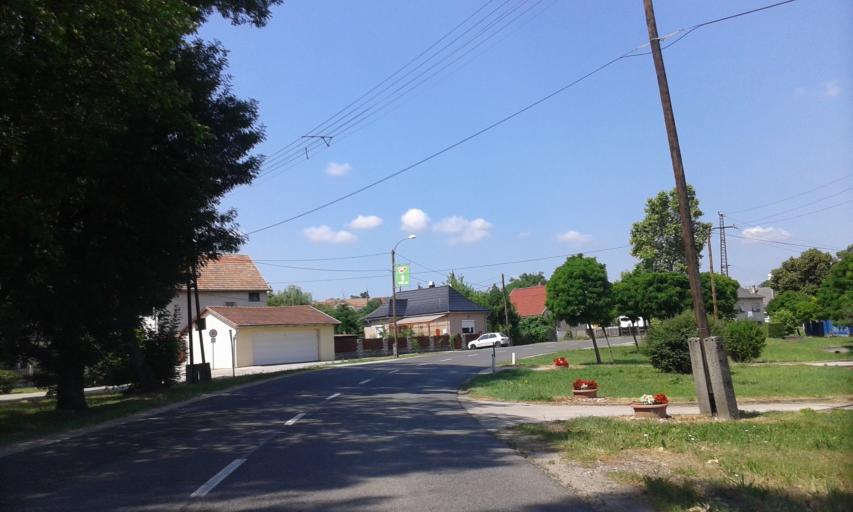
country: HU
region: Fejer
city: Bicske
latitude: 47.4920
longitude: 18.6441
